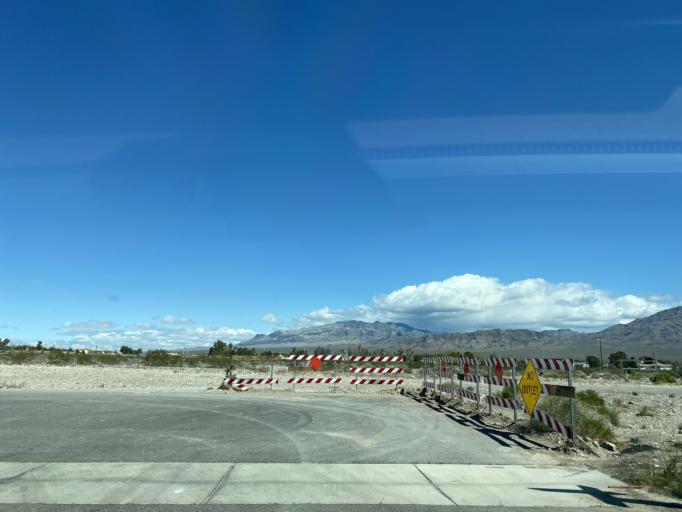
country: US
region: Nevada
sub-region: Clark County
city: North Las Vegas
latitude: 36.3211
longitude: -115.2853
